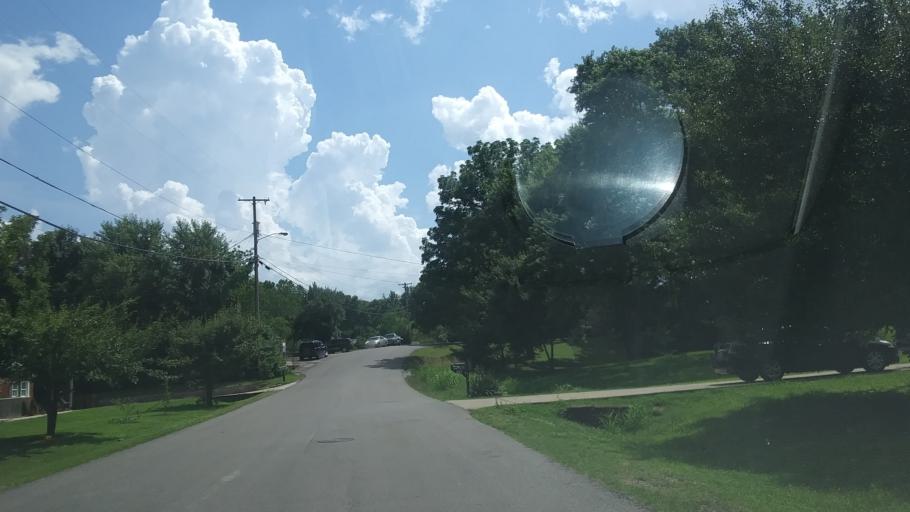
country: US
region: Tennessee
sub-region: Davidson County
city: Oak Hill
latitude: 36.0723
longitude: -86.7024
